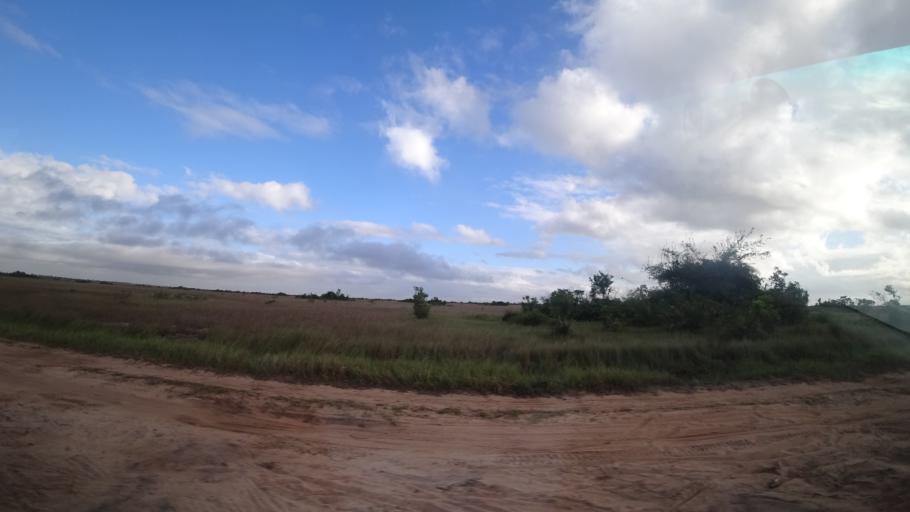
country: MZ
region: Sofala
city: Beira
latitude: -19.7028
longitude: 35.0235
